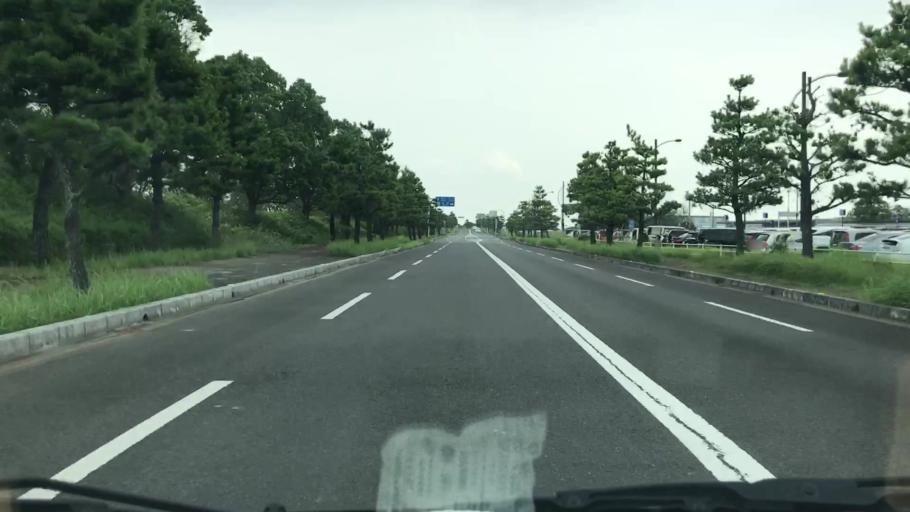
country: JP
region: Saga Prefecture
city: Okawa
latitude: 33.1549
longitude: 130.3026
